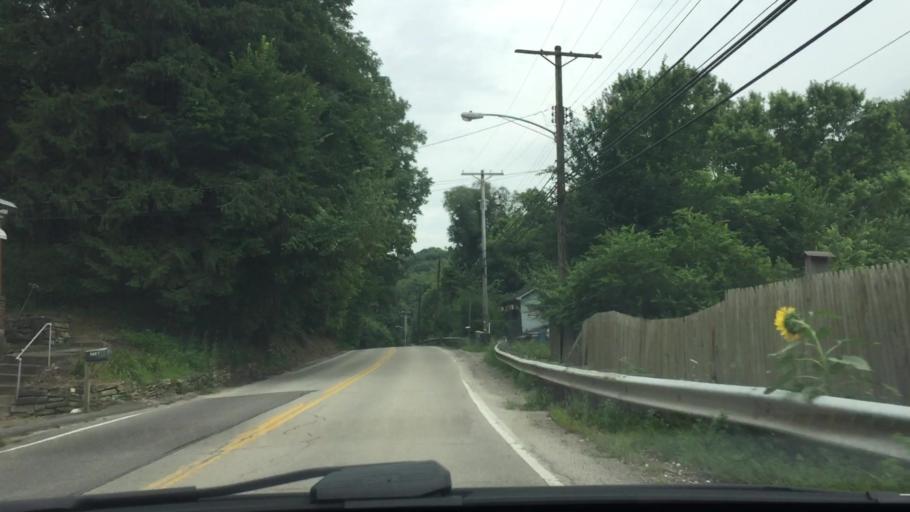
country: US
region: Pennsylvania
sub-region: Allegheny County
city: Rennerdale
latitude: 40.3752
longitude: -80.1352
